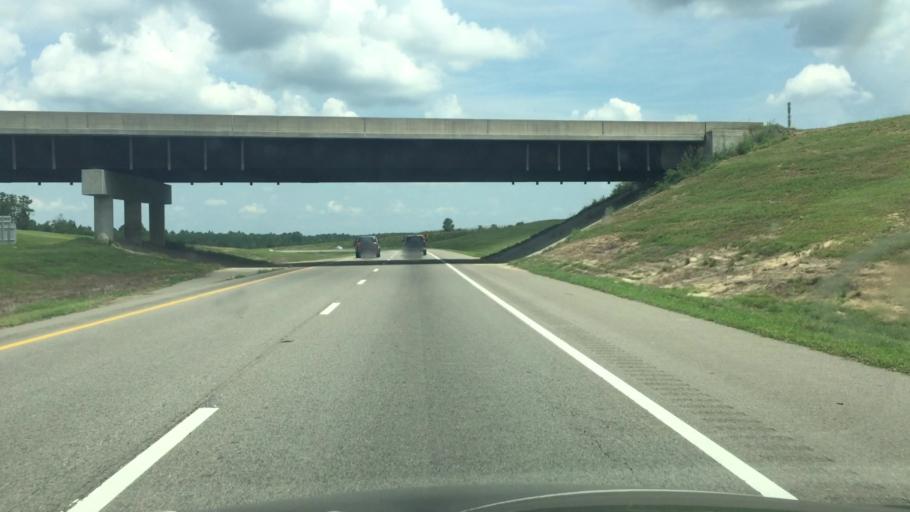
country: US
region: North Carolina
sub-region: Richmond County
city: Ellerbe
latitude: 35.1730
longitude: -79.7136
